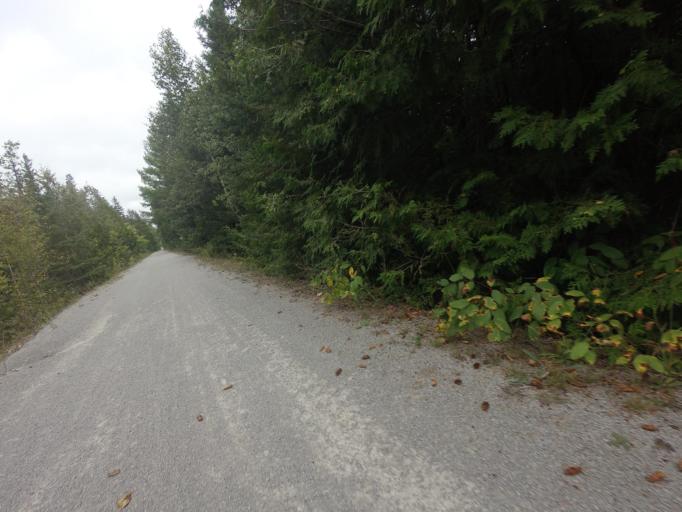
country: CA
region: Ontario
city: Uxbridge
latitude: 44.2618
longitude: -79.0263
